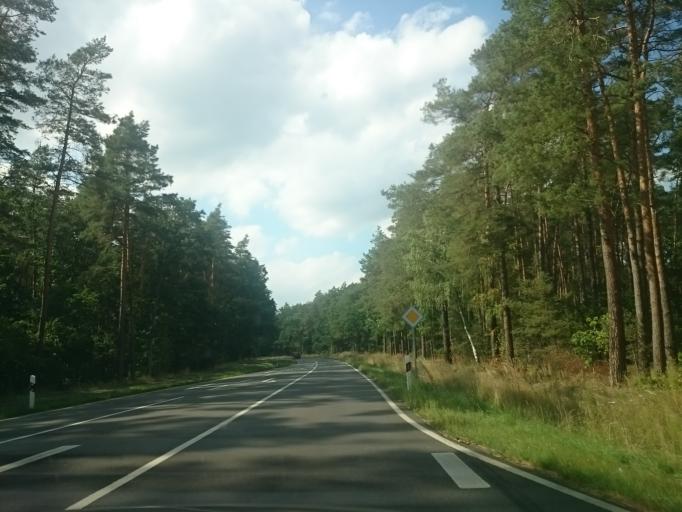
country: DE
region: Mecklenburg-Vorpommern
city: Torgelow
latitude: 53.6331
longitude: 13.9878
